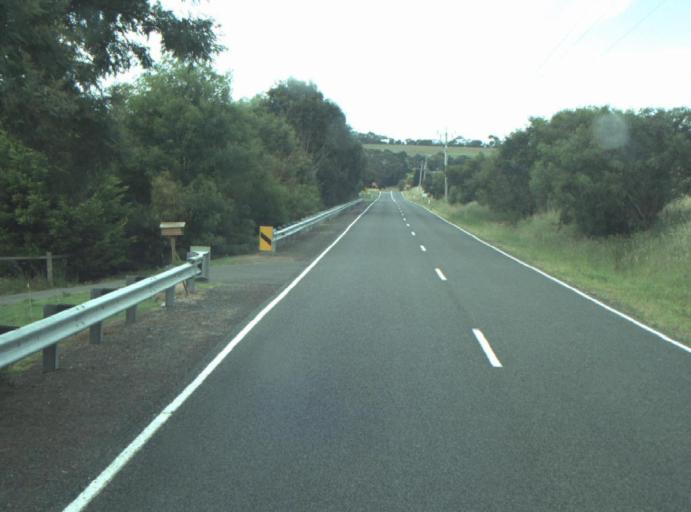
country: AU
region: Victoria
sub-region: Greater Geelong
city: Wandana Heights
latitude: -38.2029
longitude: 144.2699
